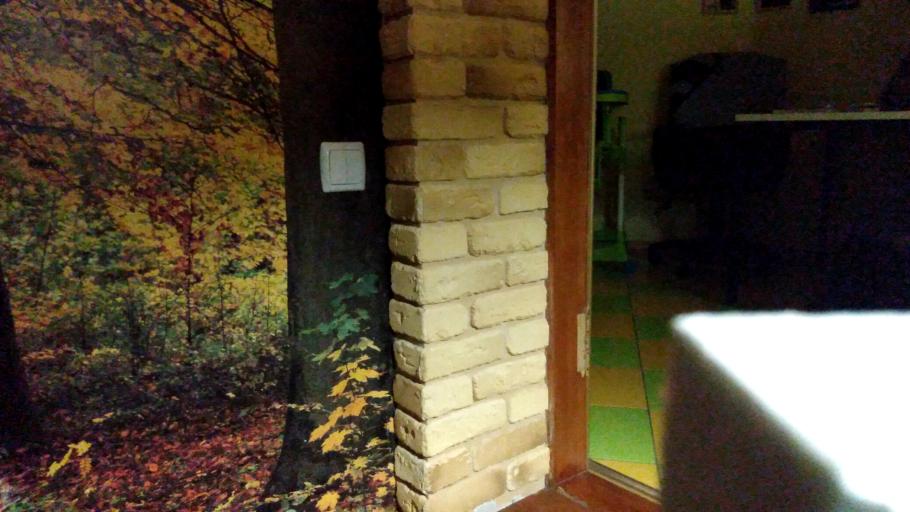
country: RU
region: Vologda
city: Lipin Bor
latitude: 61.0384
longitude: 37.9470
